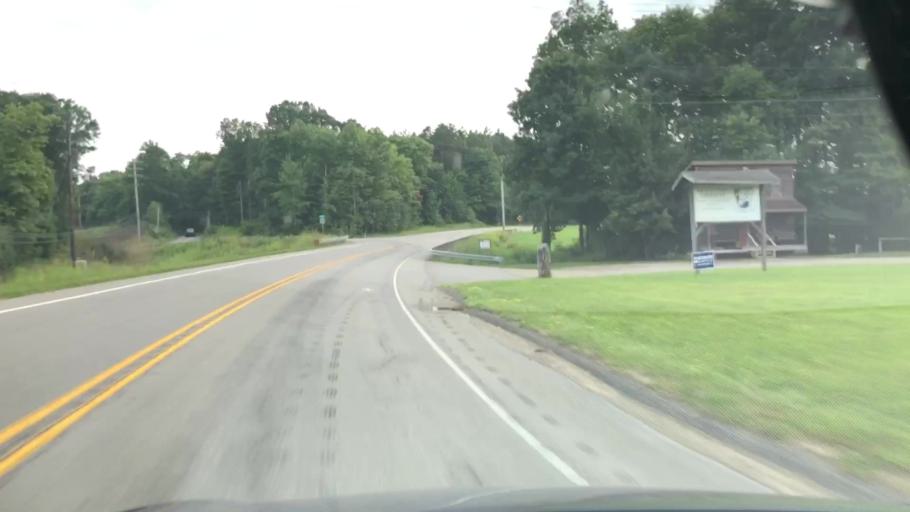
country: US
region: Pennsylvania
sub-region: Crawford County
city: Titusville
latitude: 41.5447
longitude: -79.7064
